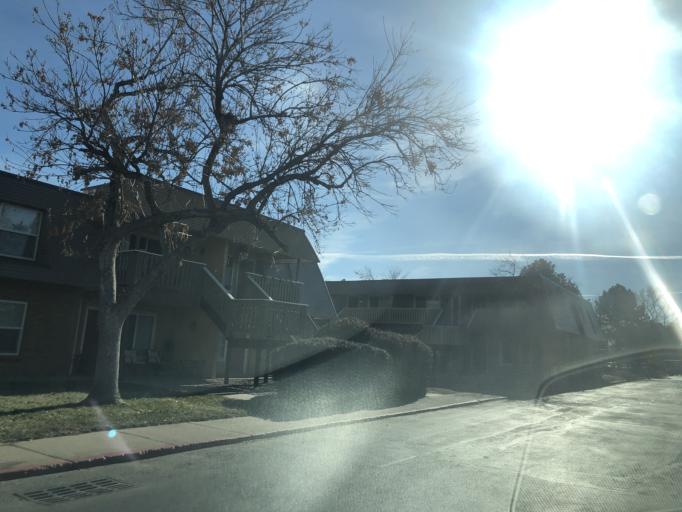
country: US
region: Colorado
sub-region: Adams County
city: Aurora
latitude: 39.7164
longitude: -104.8190
